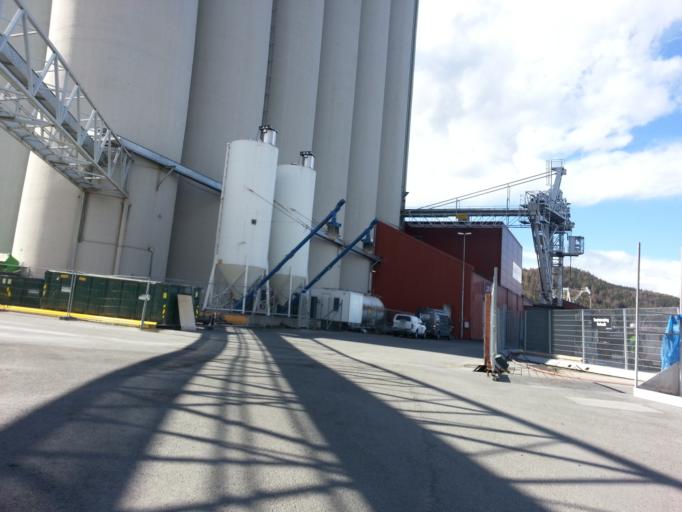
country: NO
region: Sor-Trondelag
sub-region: Trondheim
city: Trondheim
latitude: 63.4324
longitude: 10.3682
